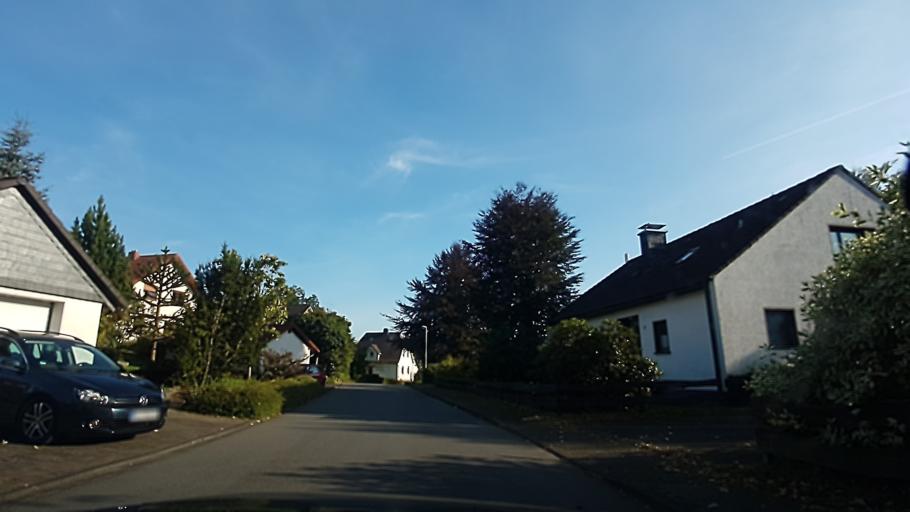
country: DE
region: North Rhine-Westphalia
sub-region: Regierungsbezirk Koln
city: Marienheide
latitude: 51.1139
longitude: 7.5047
